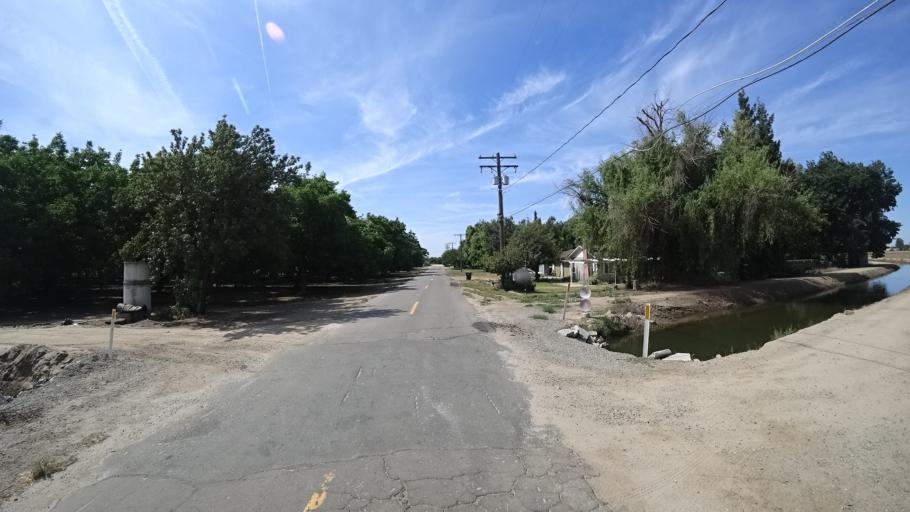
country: US
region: California
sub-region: Kings County
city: Hanford
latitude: 36.3528
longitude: -119.6222
